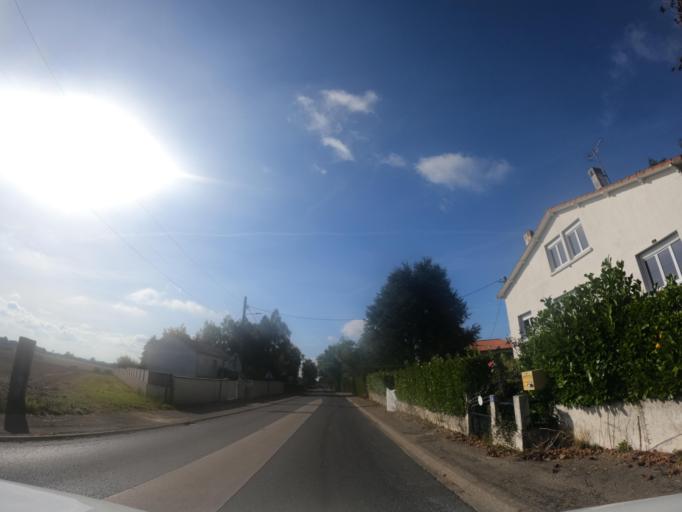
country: FR
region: Poitou-Charentes
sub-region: Departement des Deux-Sevres
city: Courlay
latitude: 46.7803
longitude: -0.5727
